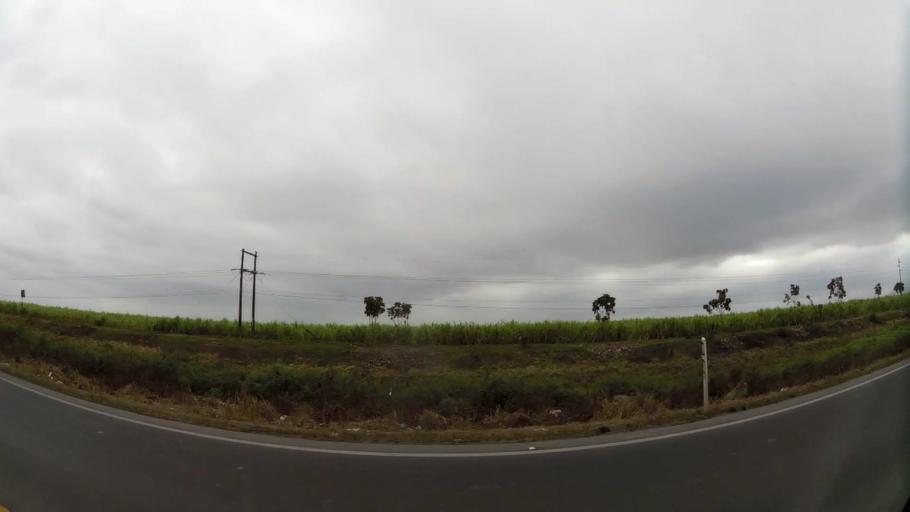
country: EC
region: Guayas
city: Coronel Marcelino Mariduena
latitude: -2.3330
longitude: -79.6357
